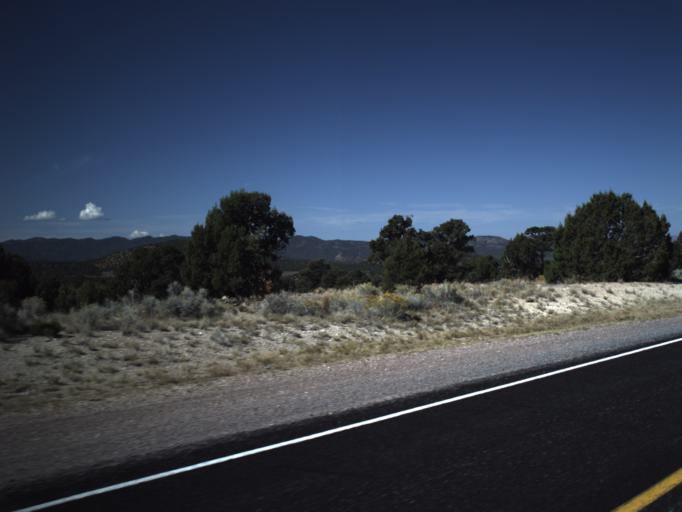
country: US
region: Utah
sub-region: Washington County
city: Enterprise
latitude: 37.6163
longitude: -113.4096
